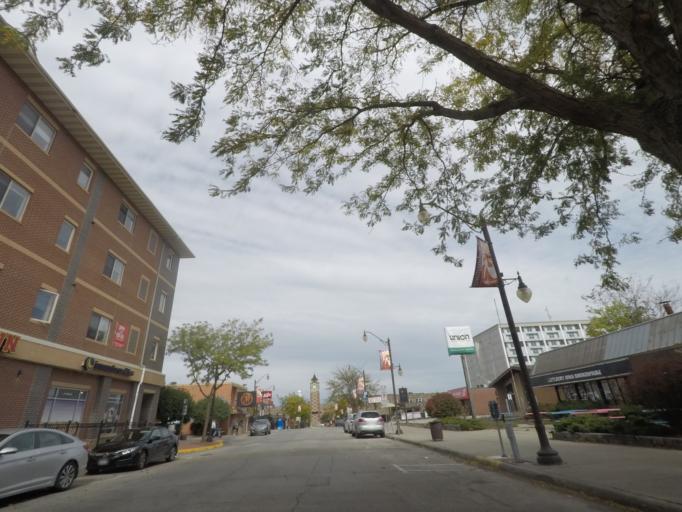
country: US
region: Iowa
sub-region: Story County
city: Ames
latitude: 42.0206
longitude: -93.6501
